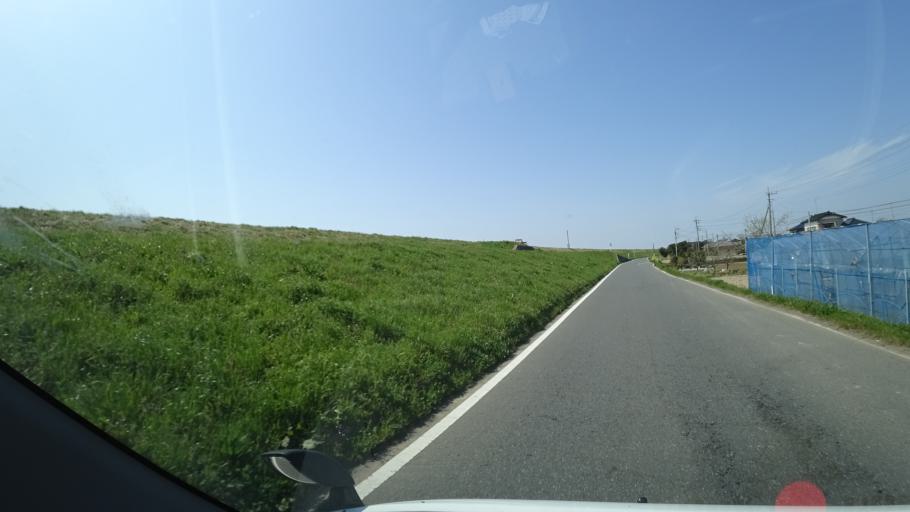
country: JP
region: Ibaraki
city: Edosaki
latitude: 35.8676
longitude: 140.3183
